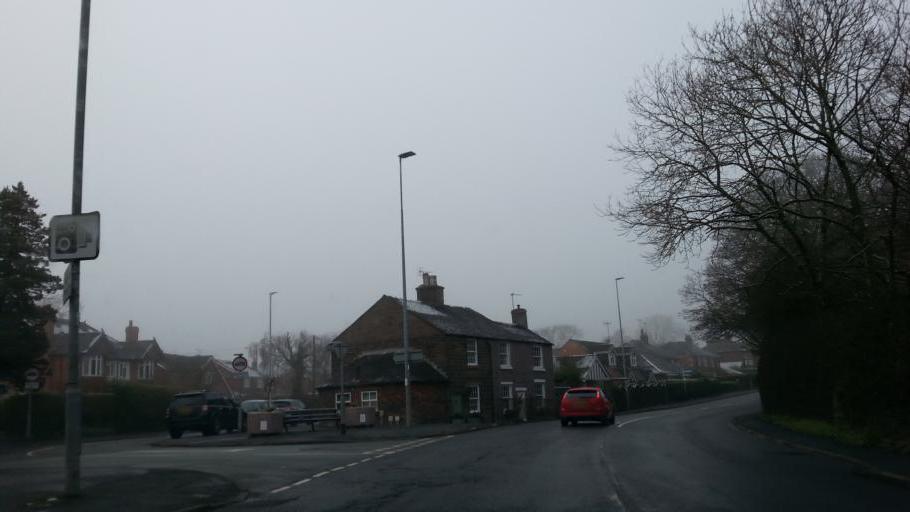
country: GB
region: England
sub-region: Staffordshire
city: Biddulph
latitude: 53.1496
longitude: -2.1806
